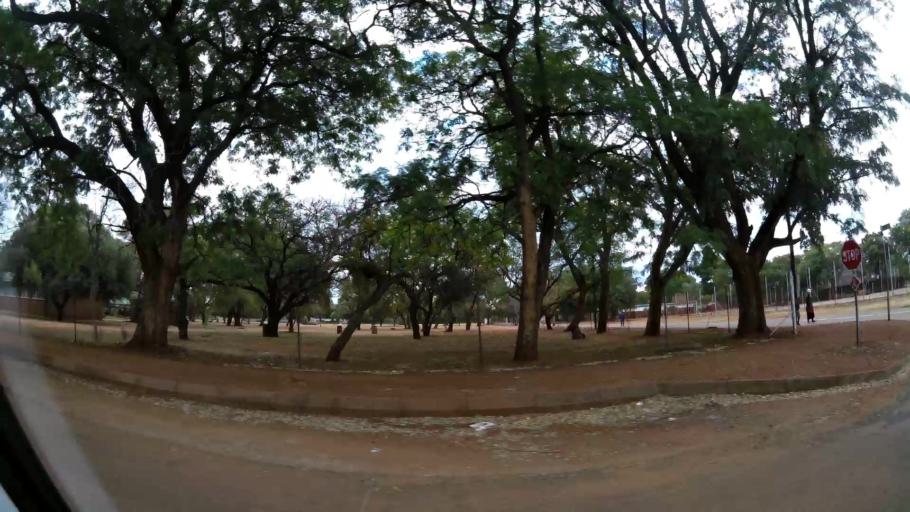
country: ZA
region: Limpopo
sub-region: Waterberg District Municipality
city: Modimolle
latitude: -24.5127
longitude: 28.7171
